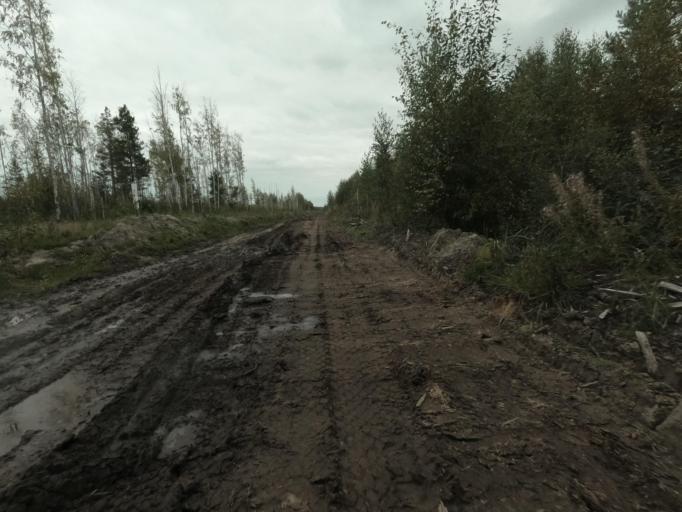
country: RU
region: St.-Petersburg
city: Sapernyy
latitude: 59.7572
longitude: 30.7096
